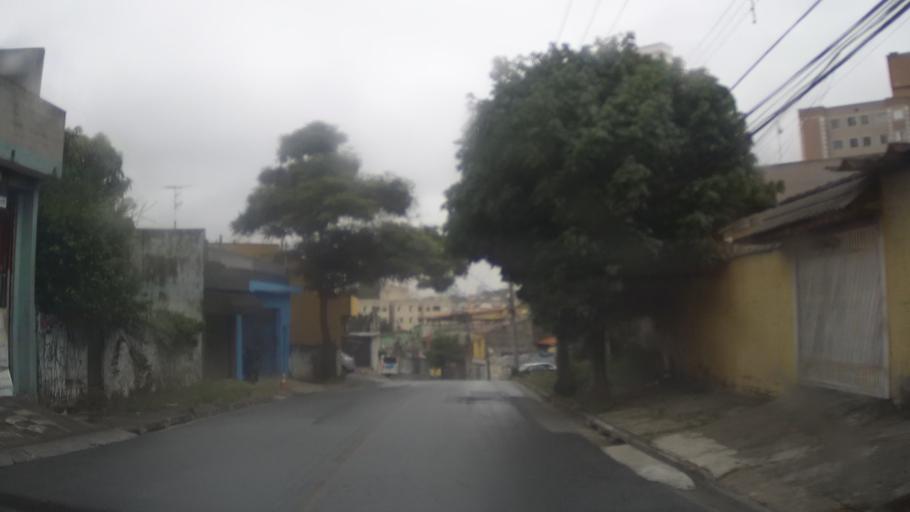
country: BR
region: Sao Paulo
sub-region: Guarulhos
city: Guarulhos
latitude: -23.4441
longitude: -46.5328
